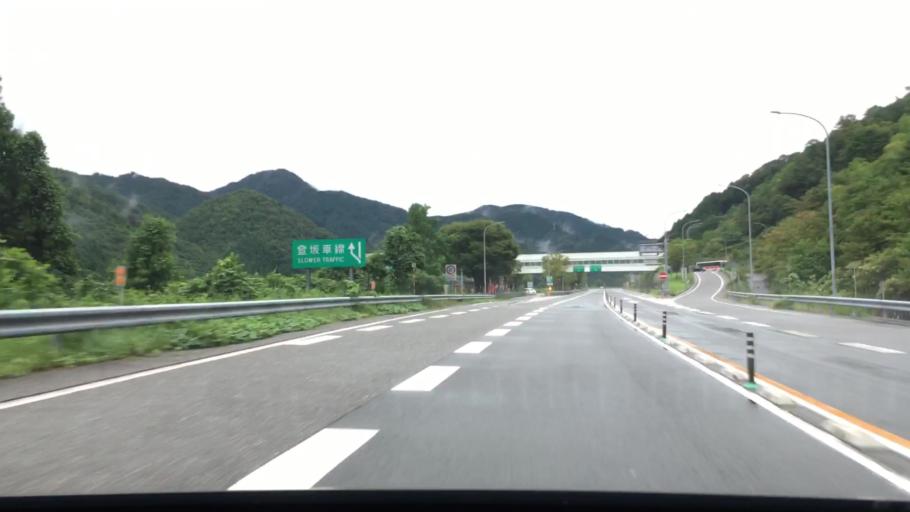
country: JP
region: Hyogo
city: Nishiwaki
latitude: 35.2152
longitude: 134.7936
